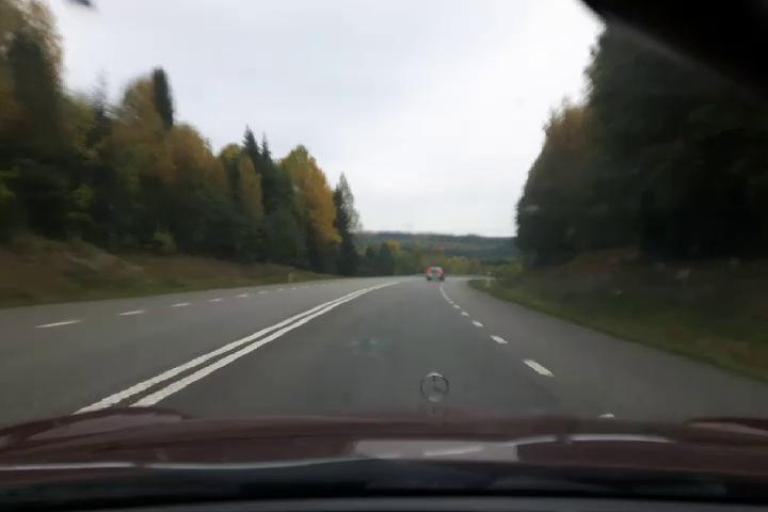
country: SE
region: Vaesternorrland
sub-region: Kramfors Kommun
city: Nordingra
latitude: 63.0315
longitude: 18.3172
